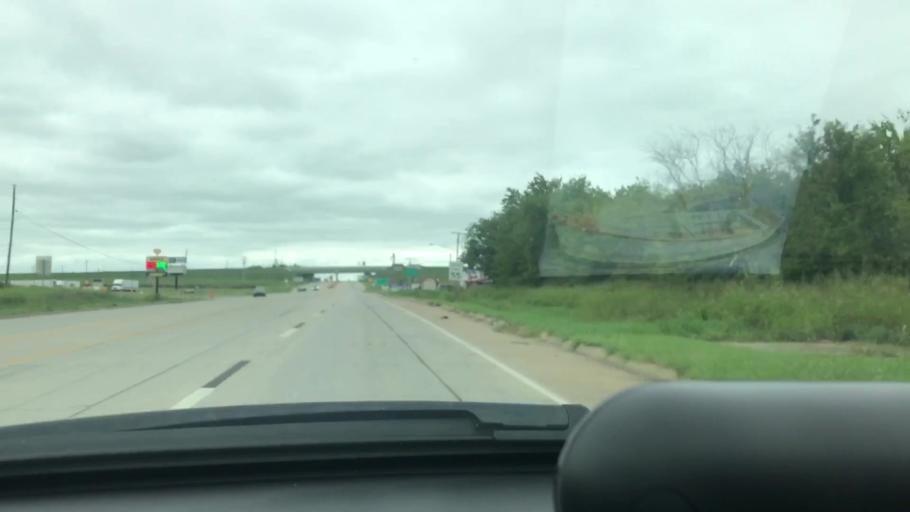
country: US
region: Oklahoma
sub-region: Mayes County
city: Chouteau
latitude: 36.1613
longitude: -95.3418
